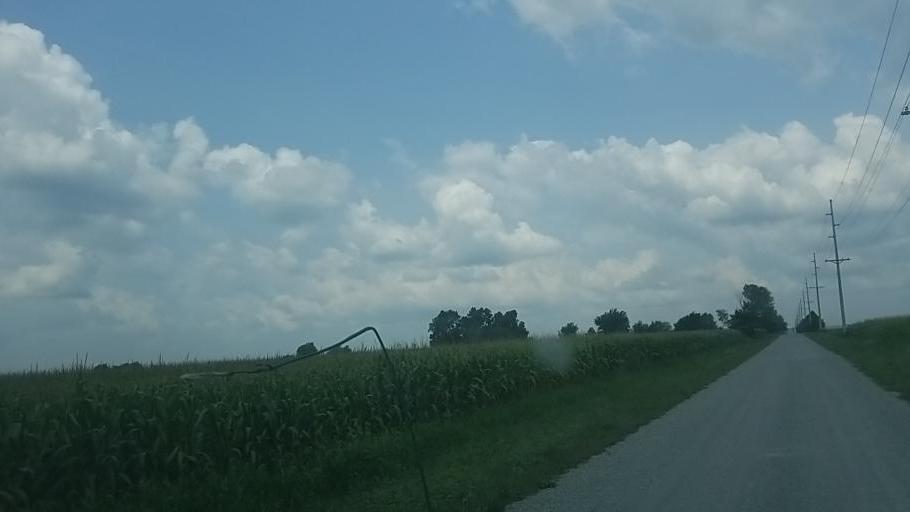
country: US
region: Ohio
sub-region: Wyandot County
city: Carey
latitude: 40.9718
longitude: -83.3049
